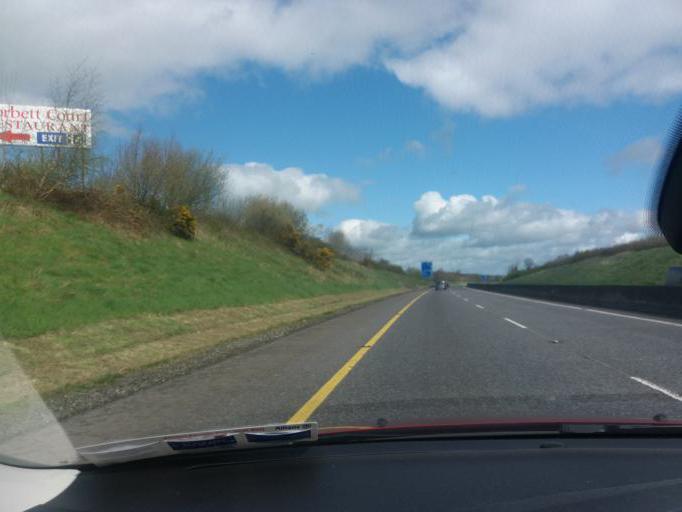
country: IE
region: Munster
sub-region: County Cork
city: Fermoy
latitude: 52.1462
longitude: -8.2654
